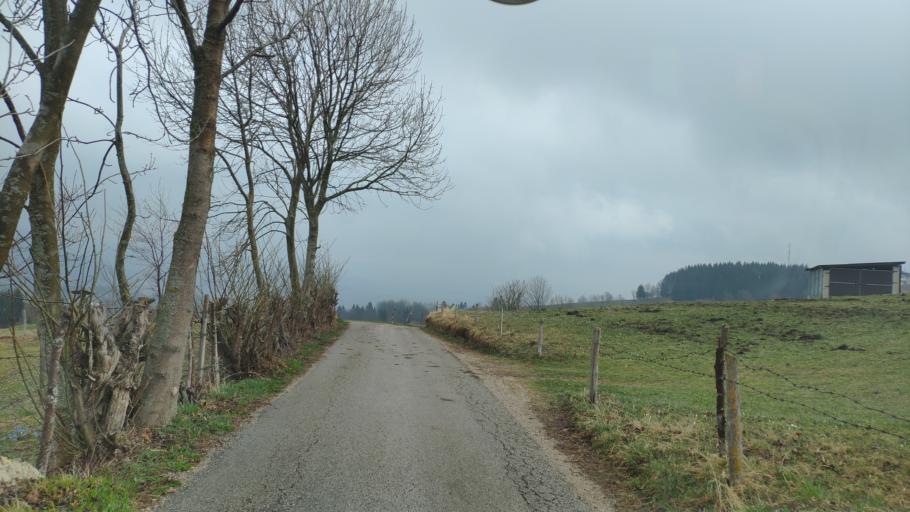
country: IT
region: Veneto
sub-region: Provincia di Vicenza
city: Rotzo
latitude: 45.8307
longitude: 11.4147
